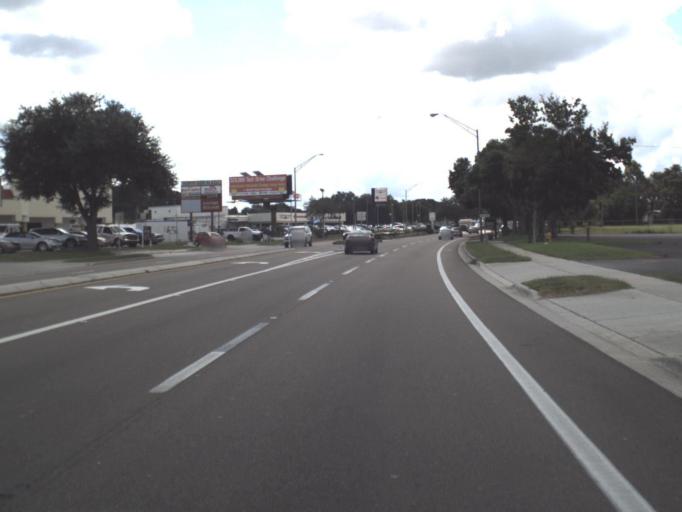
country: US
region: Florida
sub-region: Polk County
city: Lakeland
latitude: 28.0754
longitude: -81.9602
